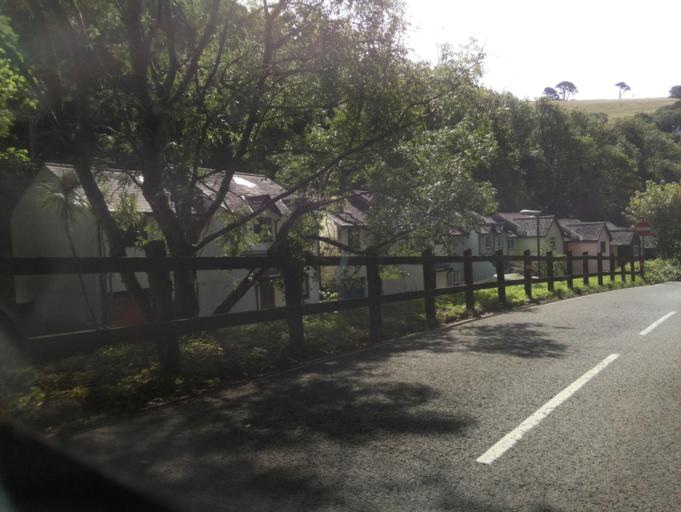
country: GB
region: England
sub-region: Devon
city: Dartmouth
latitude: 50.3547
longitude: -3.5636
